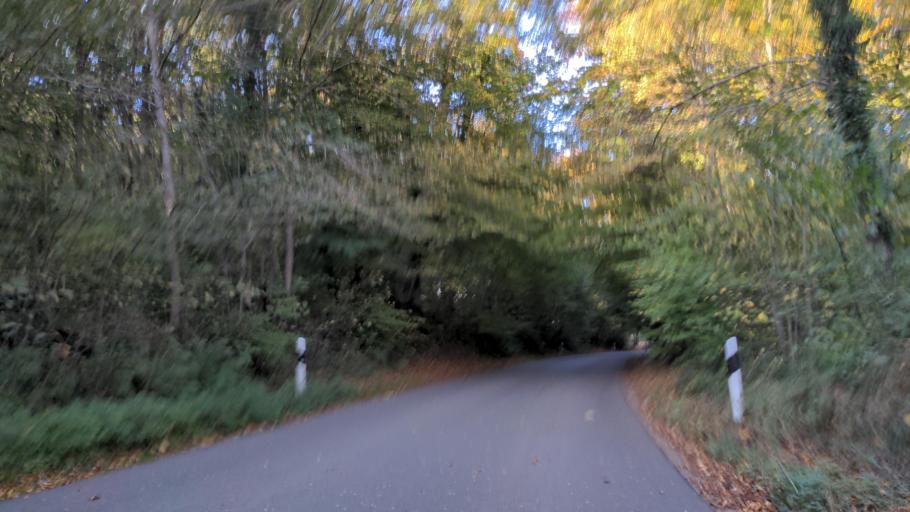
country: DE
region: Schleswig-Holstein
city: Kirchnuchel
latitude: 54.1547
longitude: 10.6686
